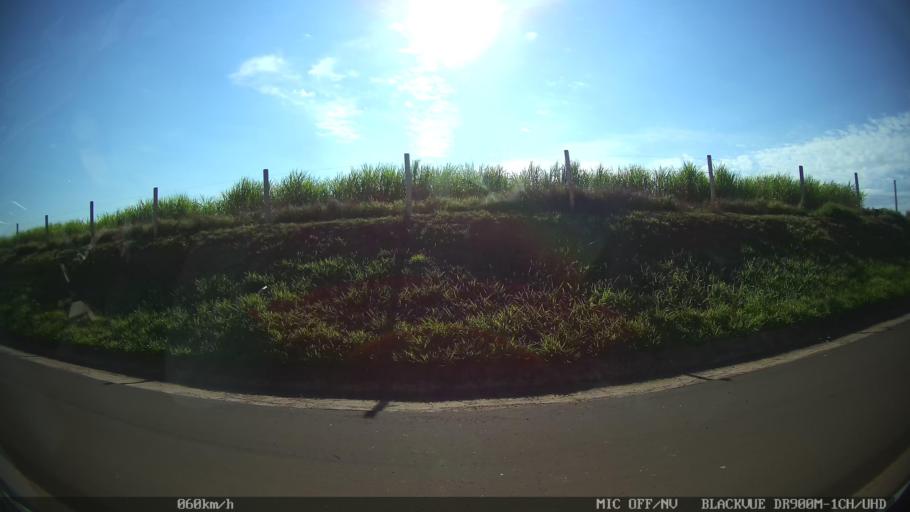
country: BR
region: Sao Paulo
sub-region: Piracicaba
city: Piracicaba
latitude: -22.6786
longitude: -47.5656
